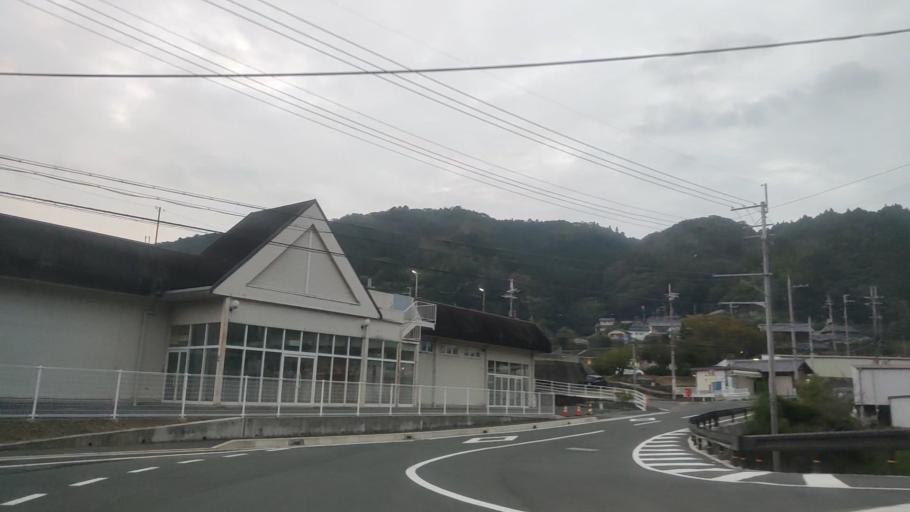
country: JP
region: Wakayama
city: Hashimoto
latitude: 34.3683
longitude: 135.6075
